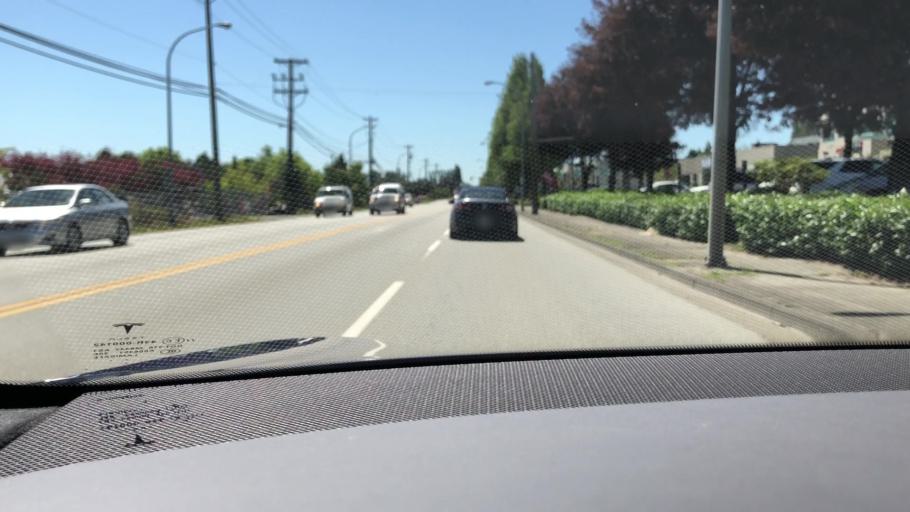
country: CA
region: British Columbia
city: Richmond
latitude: 49.1842
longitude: -123.0691
